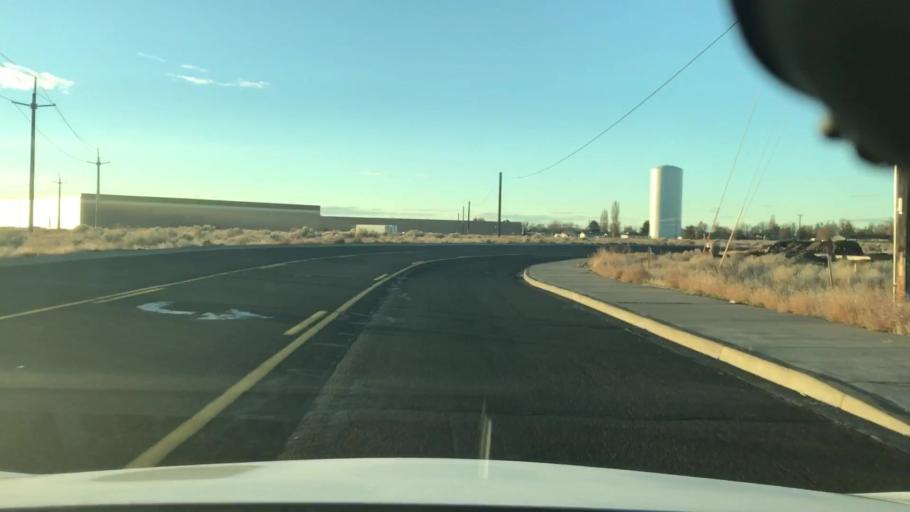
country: US
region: Washington
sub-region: Grant County
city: Moses Lake North
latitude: 47.1760
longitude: -119.3166
